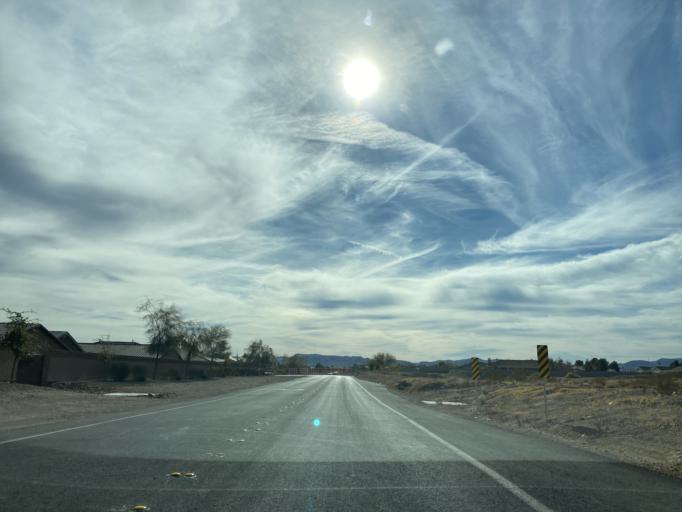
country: US
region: Nevada
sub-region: Clark County
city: Enterprise
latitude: 36.0417
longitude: -115.2168
